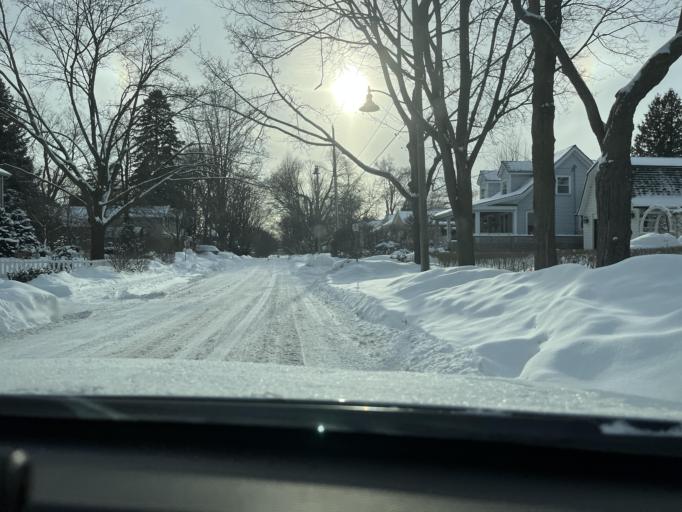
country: CA
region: Ontario
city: Oakville
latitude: 43.4464
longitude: -79.6649
